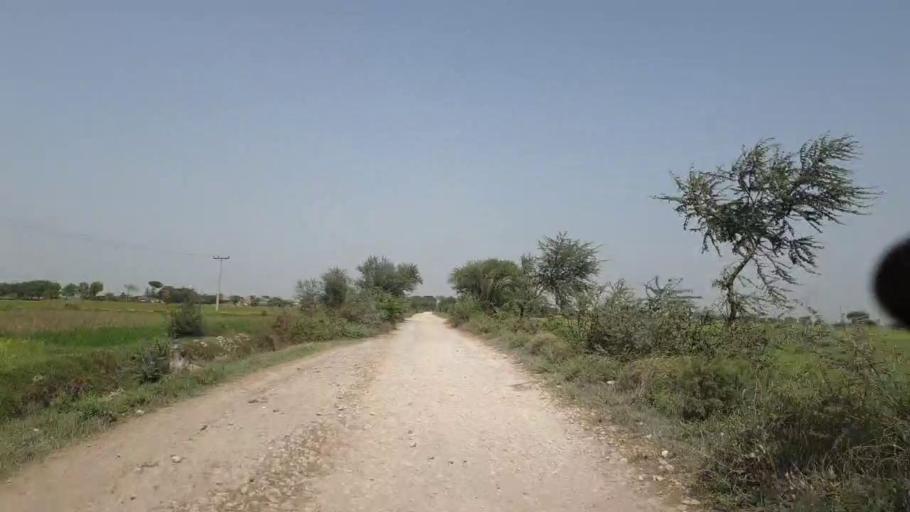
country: PK
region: Sindh
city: Matli
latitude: 25.0595
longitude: 68.6923
